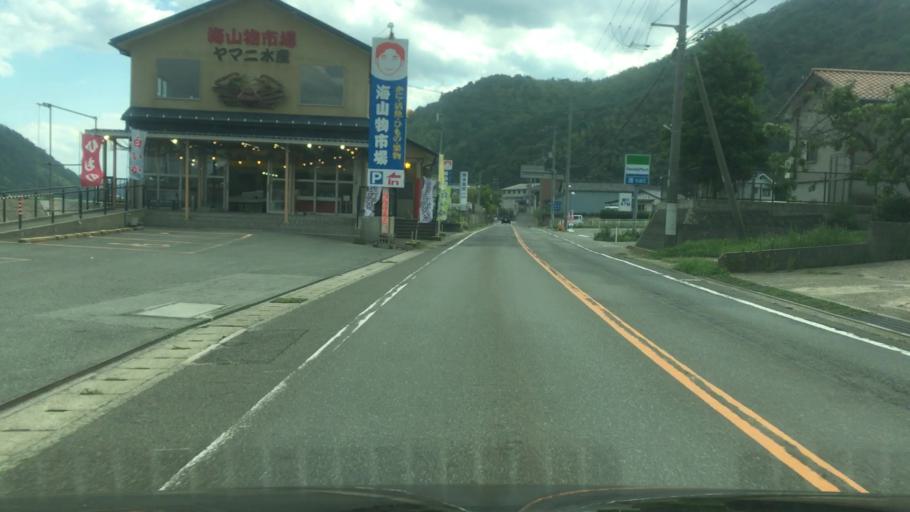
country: JP
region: Hyogo
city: Toyooka
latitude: 35.6061
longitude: 134.8028
